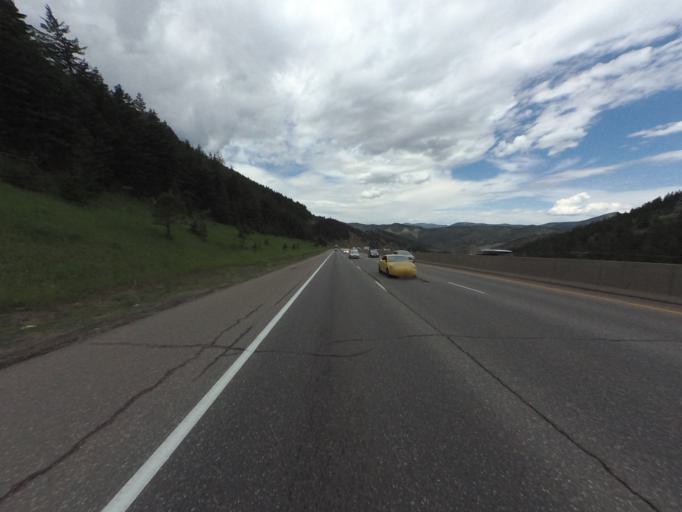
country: US
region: Colorado
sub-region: Clear Creek County
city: Idaho Springs
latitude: 39.7250
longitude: -105.4194
